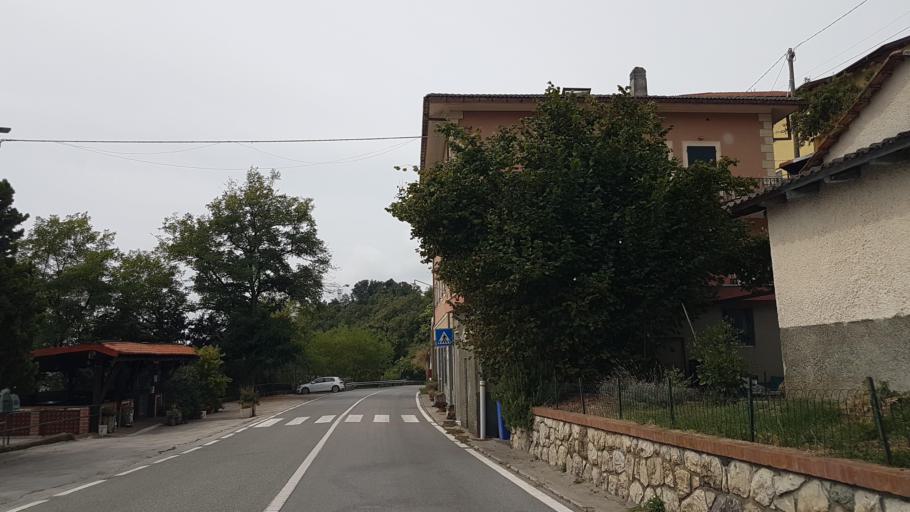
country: IT
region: Liguria
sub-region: Provincia di Genova
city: Castiglione
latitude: 44.2591
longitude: 9.5062
